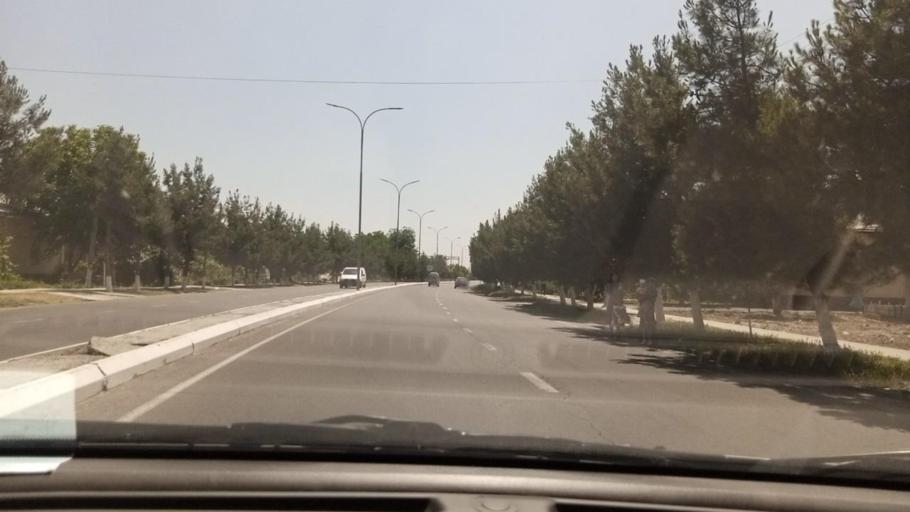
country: UZ
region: Toshkent
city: Urtaowul
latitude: 41.2102
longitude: 69.1706
